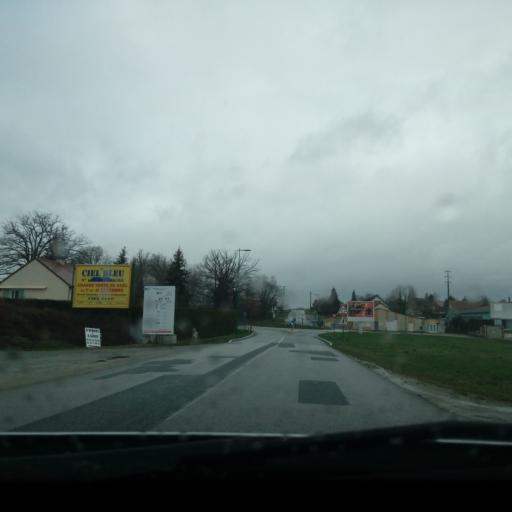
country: FR
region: Limousin
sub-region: Departement de la Creuse
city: Gueret
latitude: 46.1915
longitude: 1.8748
